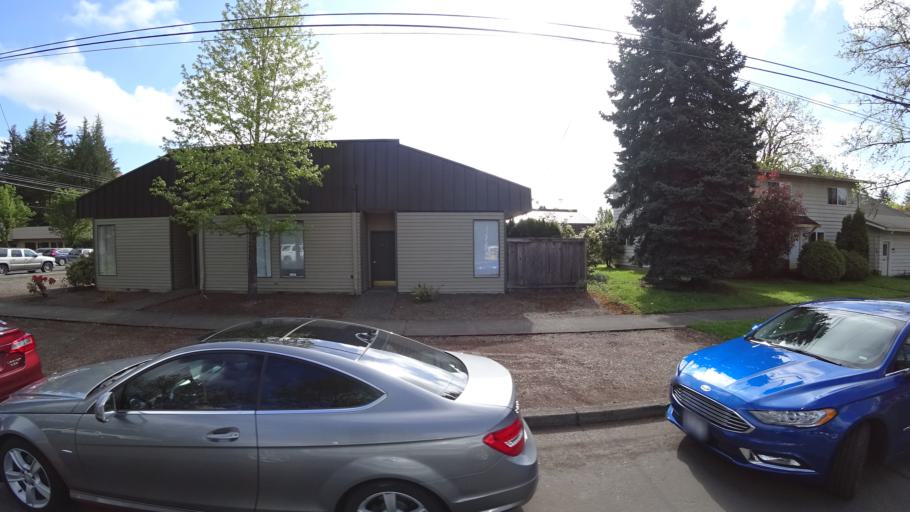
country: US
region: Oregon
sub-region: Washington County
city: Hillsboro
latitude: 45.5184
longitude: -122.9808
